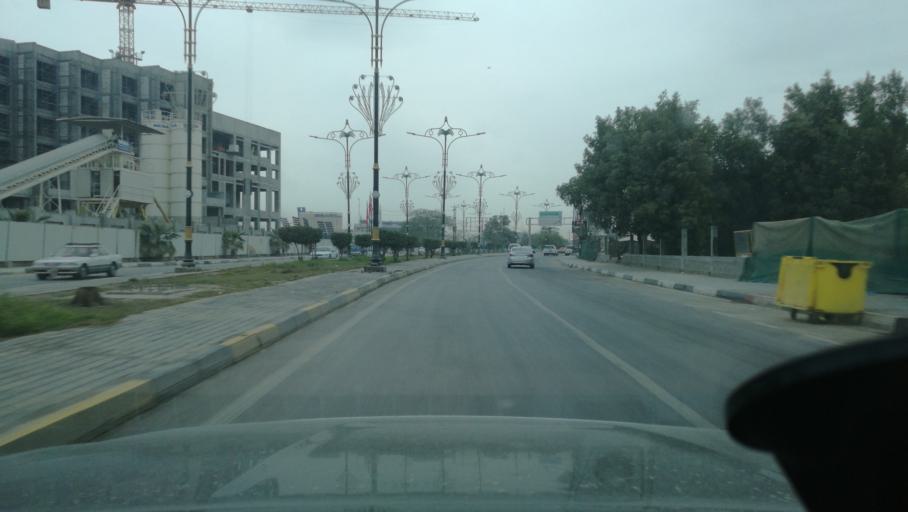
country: IQ
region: Basra Governorate
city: Al Basrah al Qadimah
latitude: 30.5017
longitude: 47.8387
